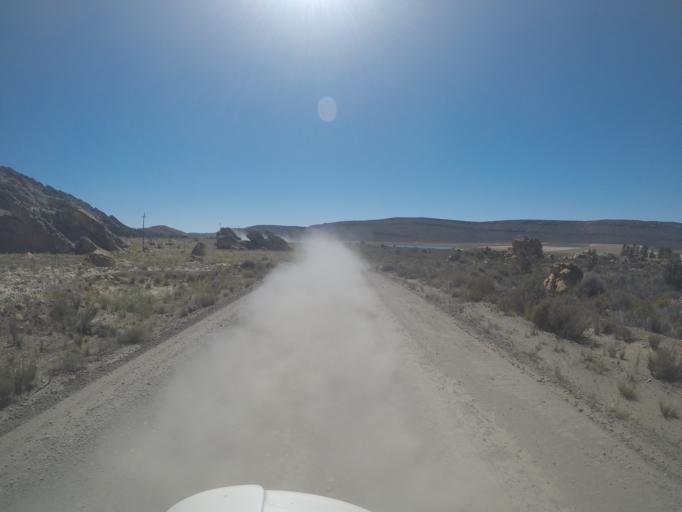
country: ZA
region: Western Cape
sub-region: Cape Winelands District Municipality
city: Ceres
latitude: -32.8444
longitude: 19.4478
